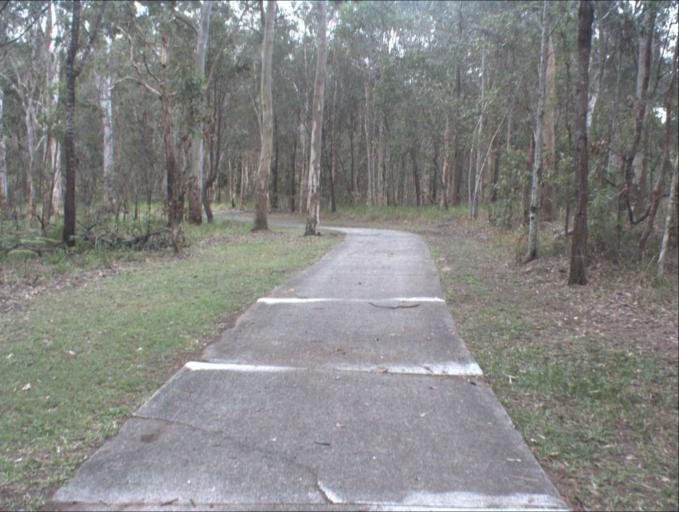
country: AU
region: Queensland
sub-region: Logan
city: Park Ridge South
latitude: -27.6952
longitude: 153.0295
